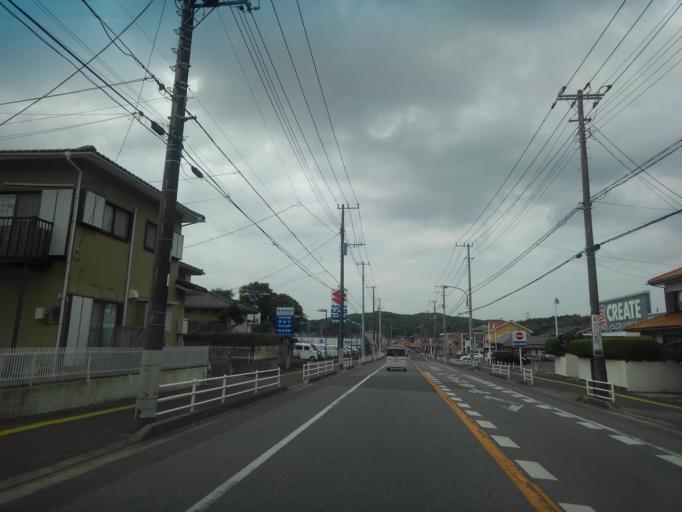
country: JP
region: Chiba
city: Kimitsu
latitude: 35.3306
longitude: 139.9185
